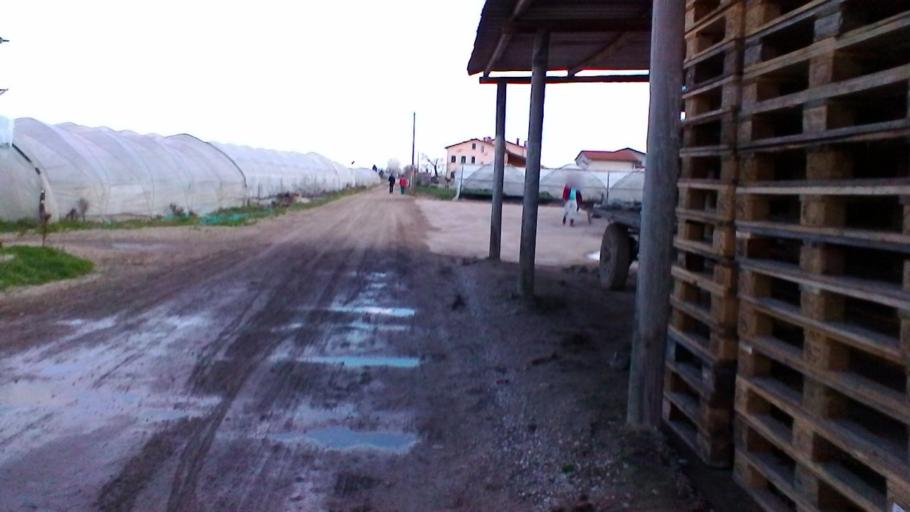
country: IT
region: Veneto
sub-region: Provincia di Verona
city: Povegliano Veronese
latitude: 45.3470
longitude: 10.8959
